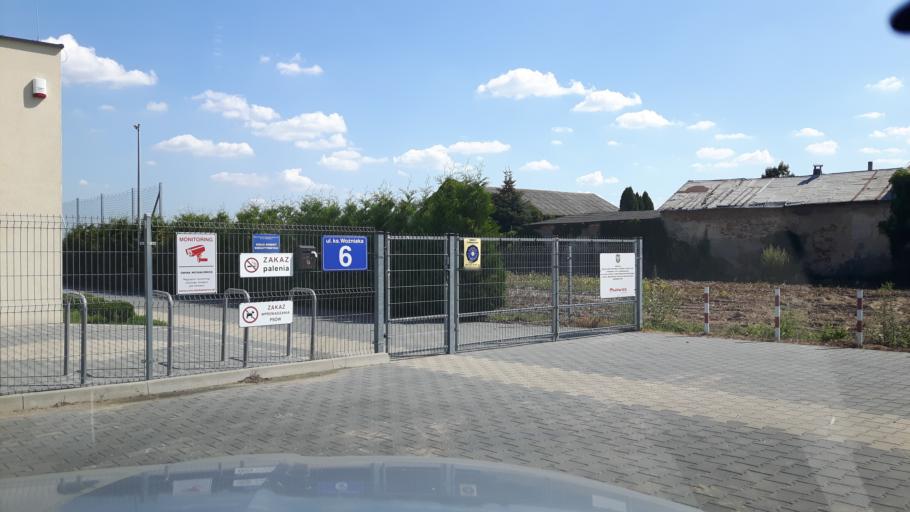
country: PL
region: Masovian Voivodeship
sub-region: Powiat pruszkowski
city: Komorow
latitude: 52.1344
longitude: 20.8539
